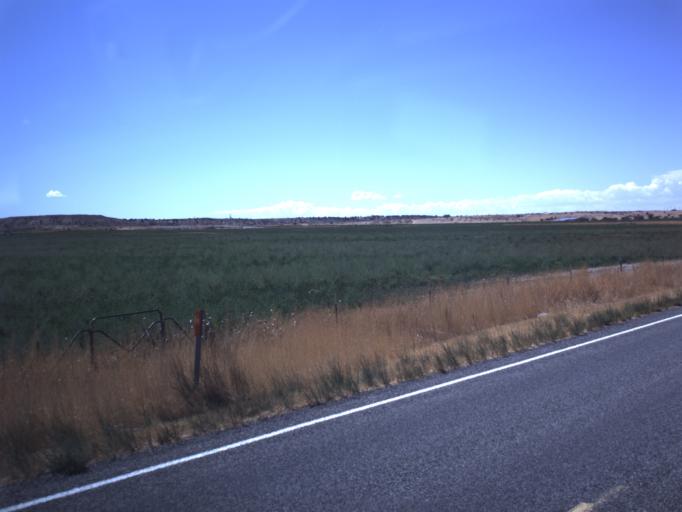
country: US
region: Utah
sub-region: Millard County
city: Delta
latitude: 39.5392
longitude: -112.2501
